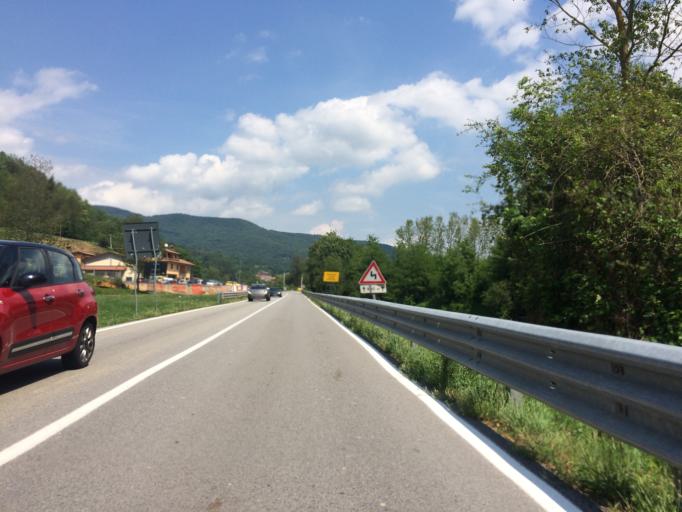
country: IT
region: Piedmont
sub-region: Provincia di Cuneo
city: Priola
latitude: 44.2496
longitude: 8.0216
